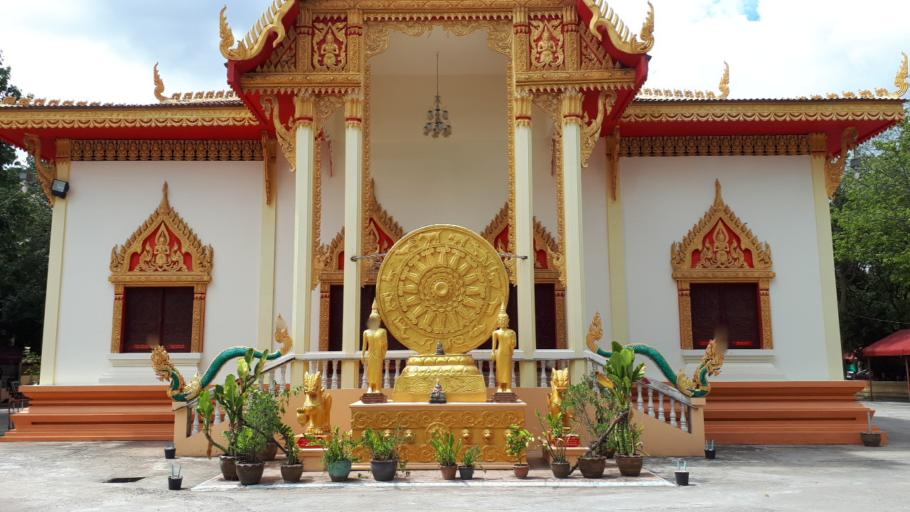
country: TH
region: Changwat Ubon Ratchathani
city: Ubon Ratchathani
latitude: 15.2813
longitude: 104.8305
